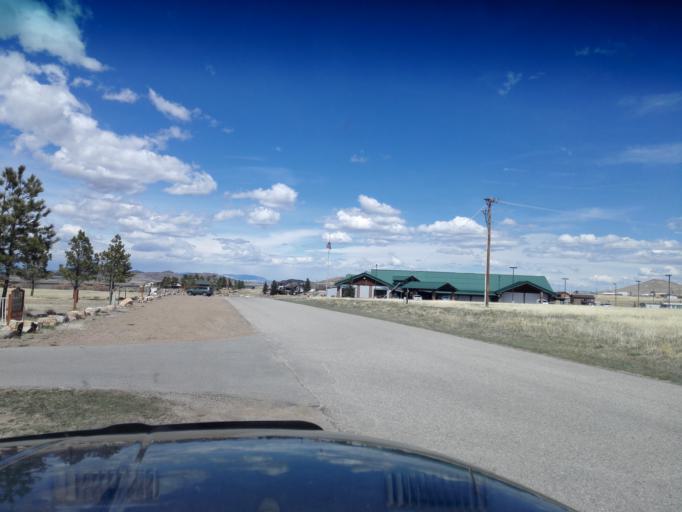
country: US
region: Colorado
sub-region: Custer County
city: Westcliffe
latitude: 38.1351
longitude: -105.4710
